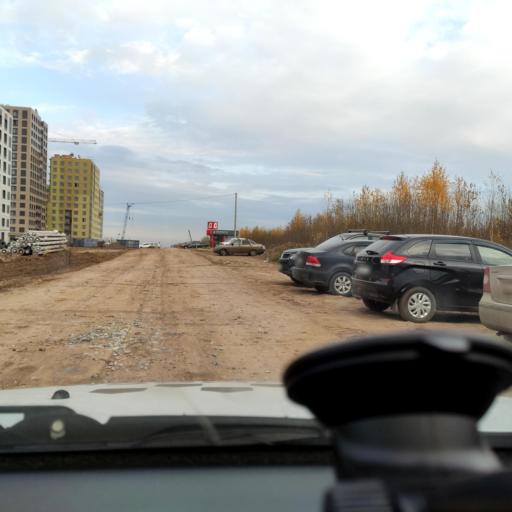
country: RU
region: Perm
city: Perm
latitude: 58.0097
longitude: 56.3333
